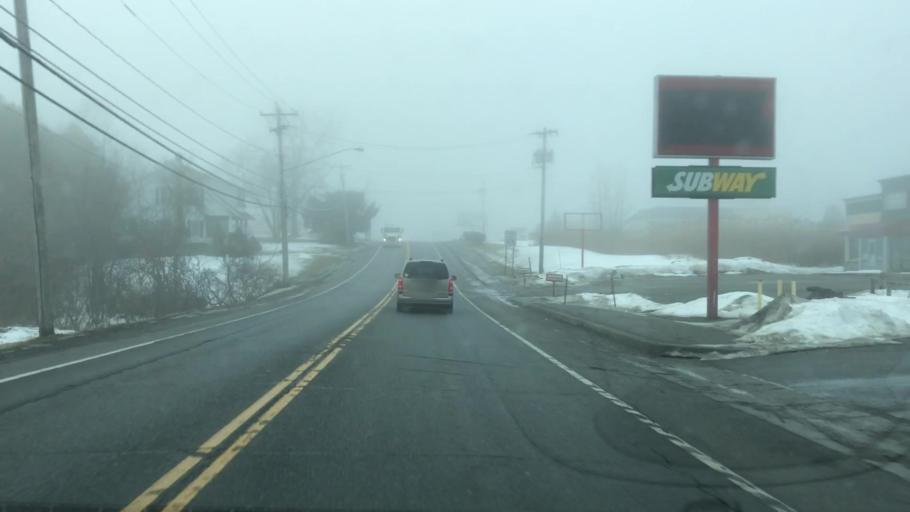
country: US
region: New York
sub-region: Washington County
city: Whitehall
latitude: 43.5404
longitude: -73.4088
